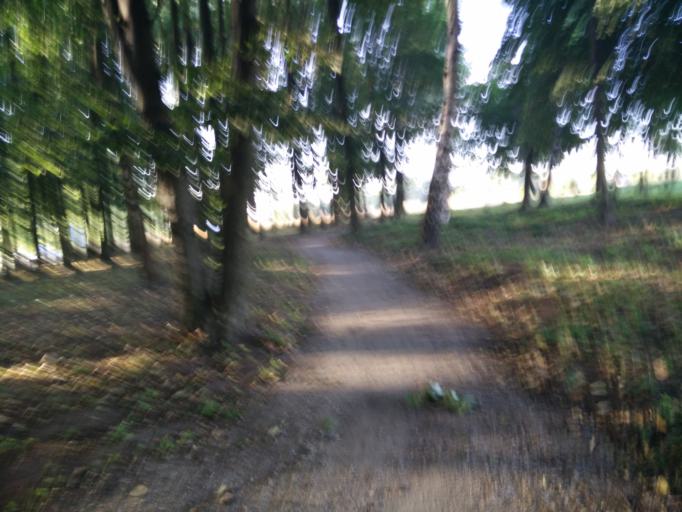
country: PL
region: Greater Poland Voivodeship
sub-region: Powiat sredzki
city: Sroda Wielkopolska
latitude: 52.2393
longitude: 17.2939
